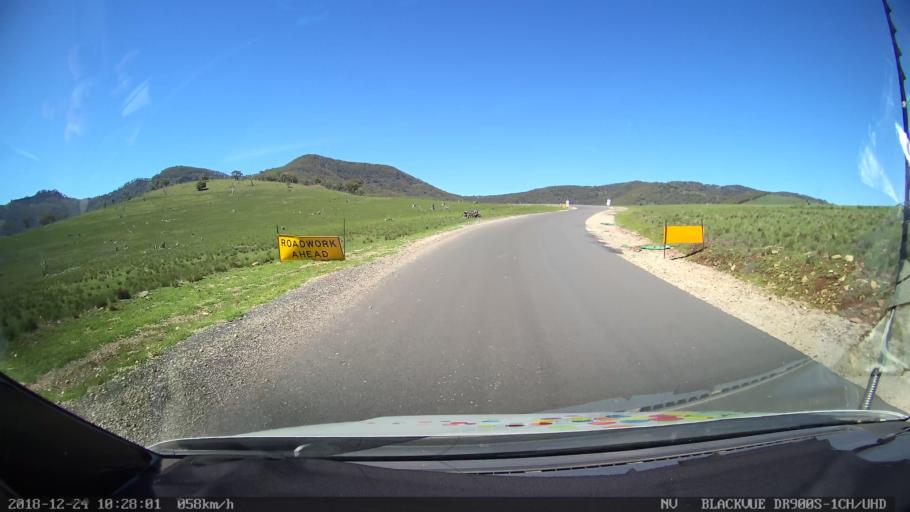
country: AU
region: New South Wales
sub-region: Liverpool Plains
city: Quirindi
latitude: -31.8237
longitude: 150.5339
